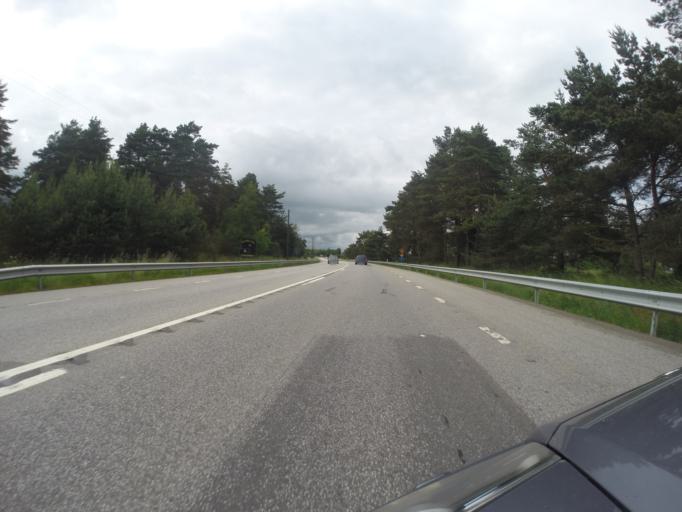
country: SE
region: Skane
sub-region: Kavlinge Kommun
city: Hofterup
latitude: 55.8335
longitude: 12.9609
